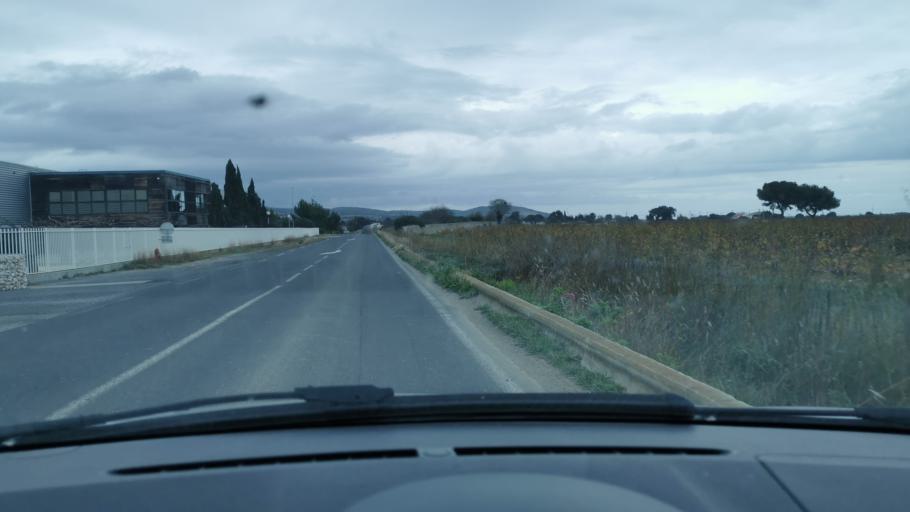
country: FR
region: Languedoc-Roussillon
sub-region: Departement de l'Herault
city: Balaruc-les-Bains
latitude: 43.4375
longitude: 3.7095
